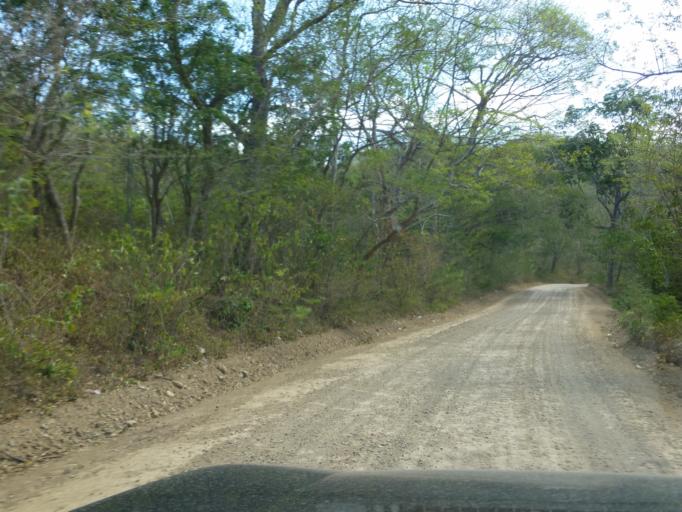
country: CR
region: Guanacaste
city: La Cruz
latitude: 11.1192
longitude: -85.7664
